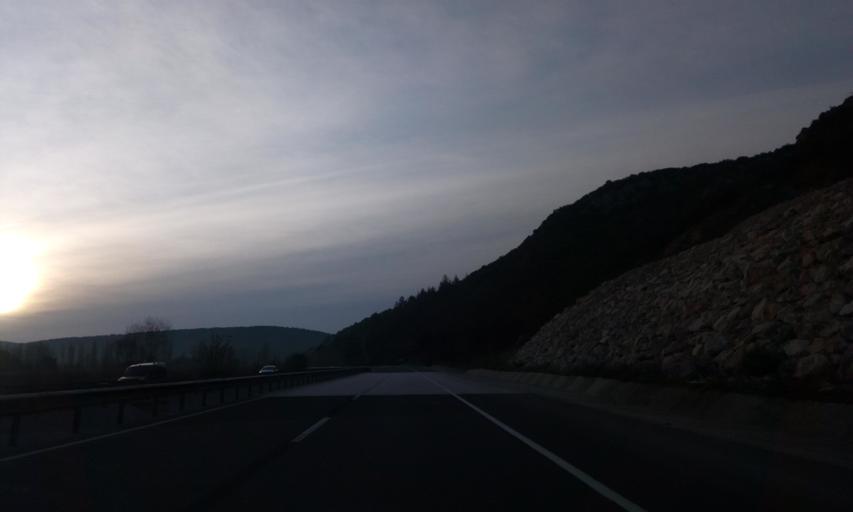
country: TR
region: Bilecik
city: Bilecik
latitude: 40.1524
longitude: 30.0214
